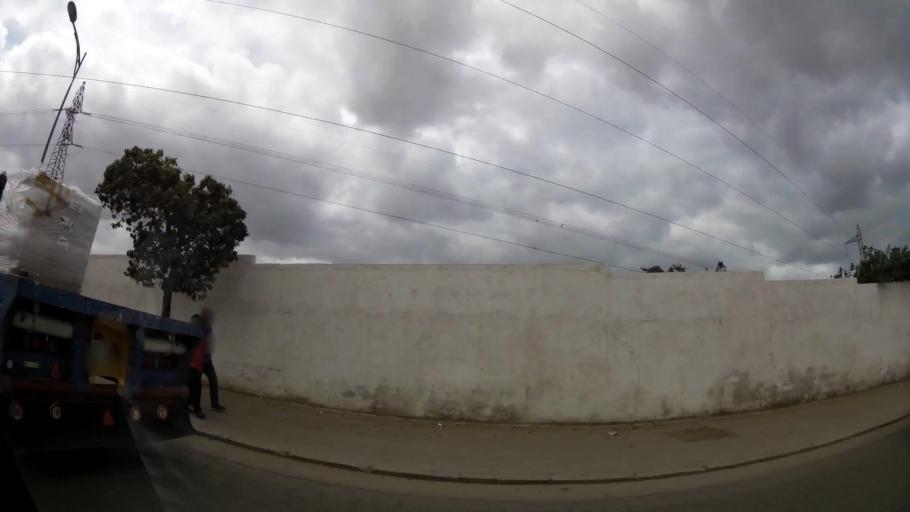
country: MA
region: Grand Casablanca
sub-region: Casablanca
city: Casablanca
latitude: 33.5862
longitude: -7.5461
